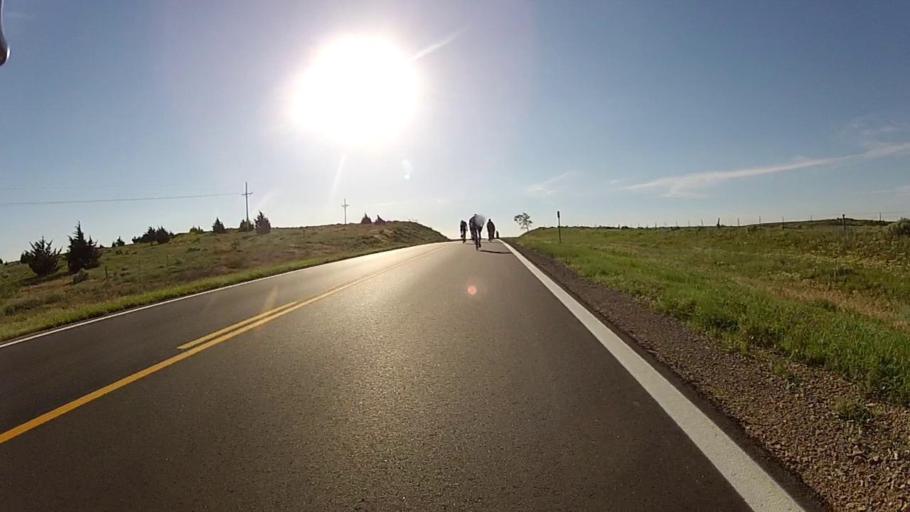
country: US
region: Kansas
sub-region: Comanche County
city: Coldwater
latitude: 37.2809
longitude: -99.0376
